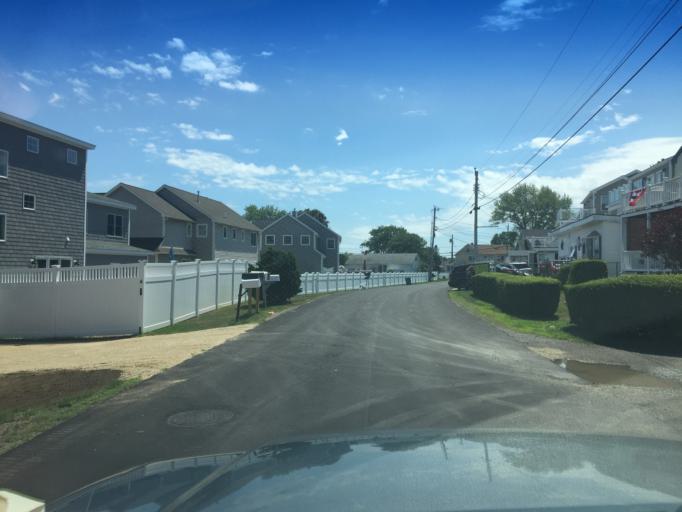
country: US
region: Maine
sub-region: York County
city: York Beach
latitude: 43.1537
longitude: -70.6256
